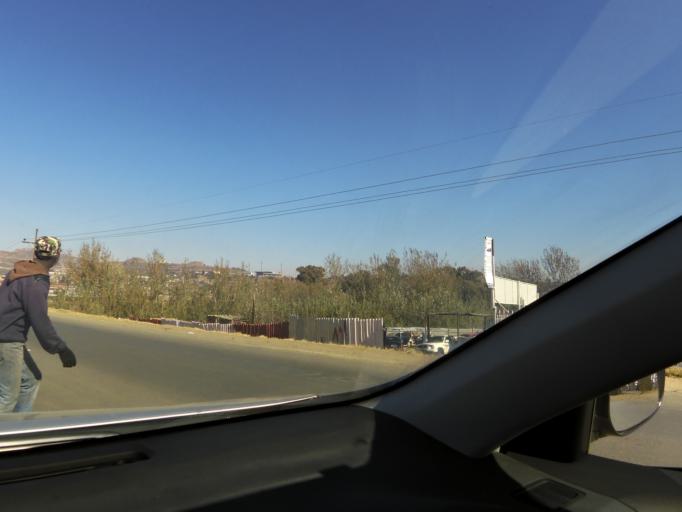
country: LS
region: Maseru
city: Maseru
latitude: -29.3017
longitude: 27.5167
